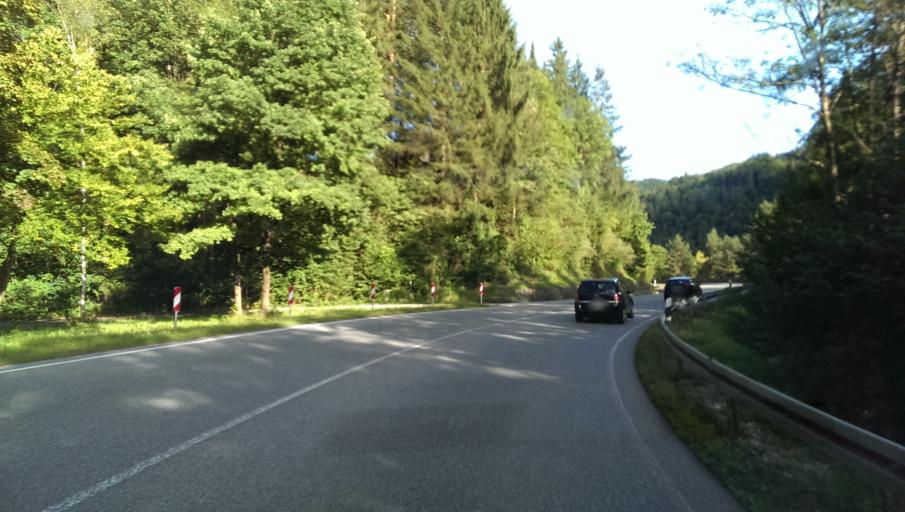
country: DE
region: Bavaria
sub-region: Upper Bavaria
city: Garmisch-Partenkirchen
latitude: 47.4857
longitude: 11.1328
